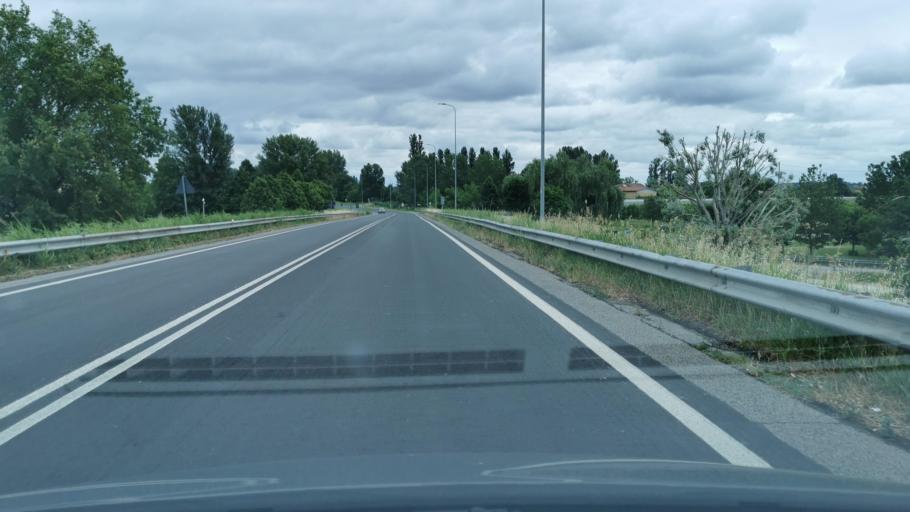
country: IT
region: Emilia-Romagna
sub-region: Provincia di Ravenna
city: Granarolo
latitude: 44.3695
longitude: 11.9408
